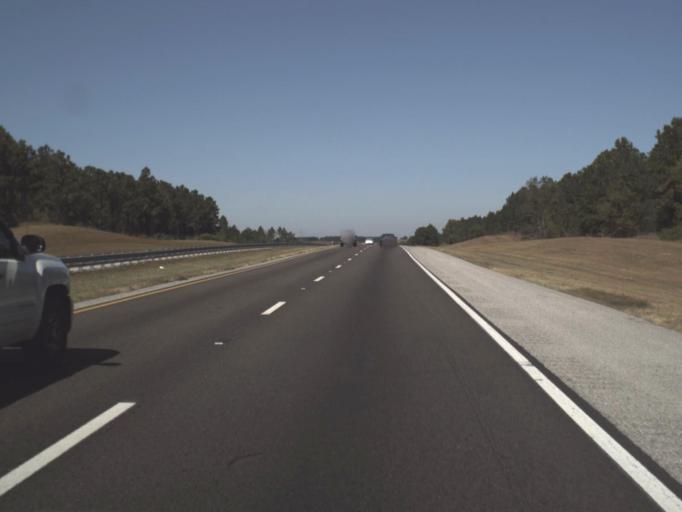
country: US
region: Florida
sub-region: Lake County
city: Minneola
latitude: 28.5988
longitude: -81.7186
